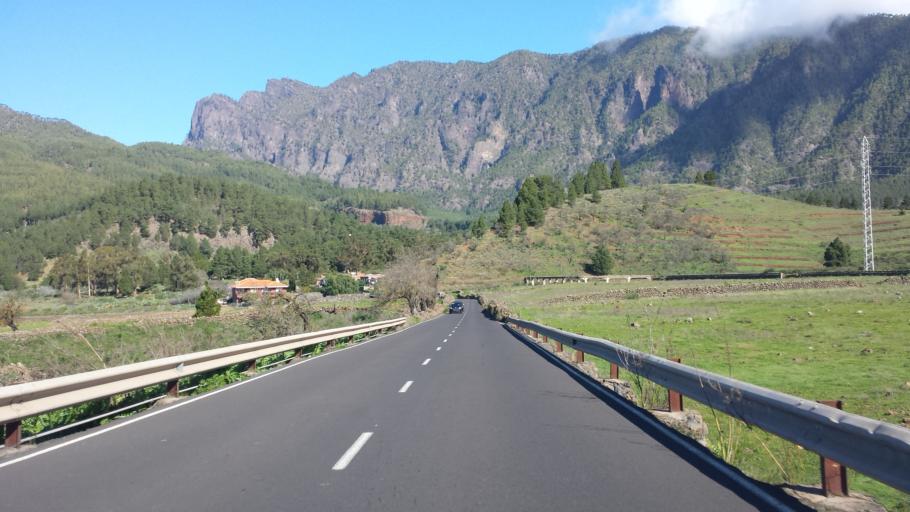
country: ES
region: Canary Islands
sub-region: Provincia de Santa Cruz de Tenerife
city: El Paso
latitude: 28.6574
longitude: -17.8520
